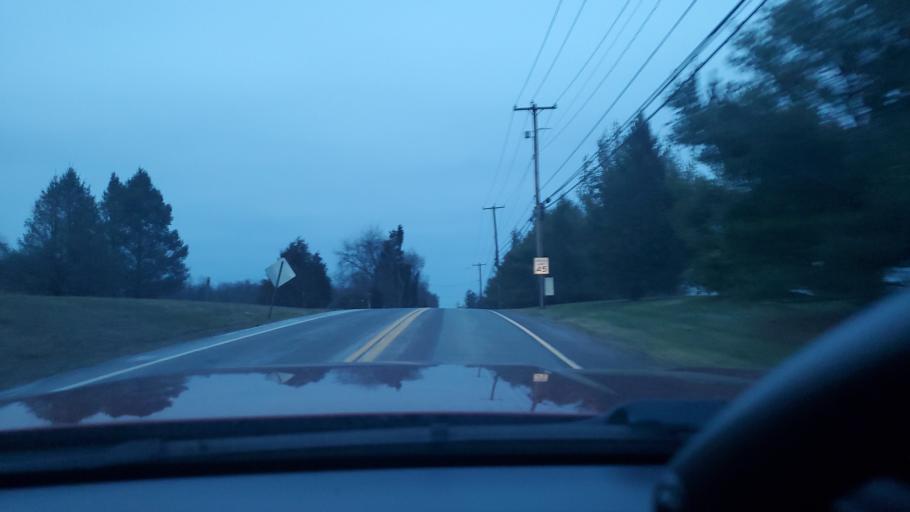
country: US
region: Pennsylvania
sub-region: Montgomery County
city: Schwenksville
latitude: 40.2378
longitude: -75.4771
